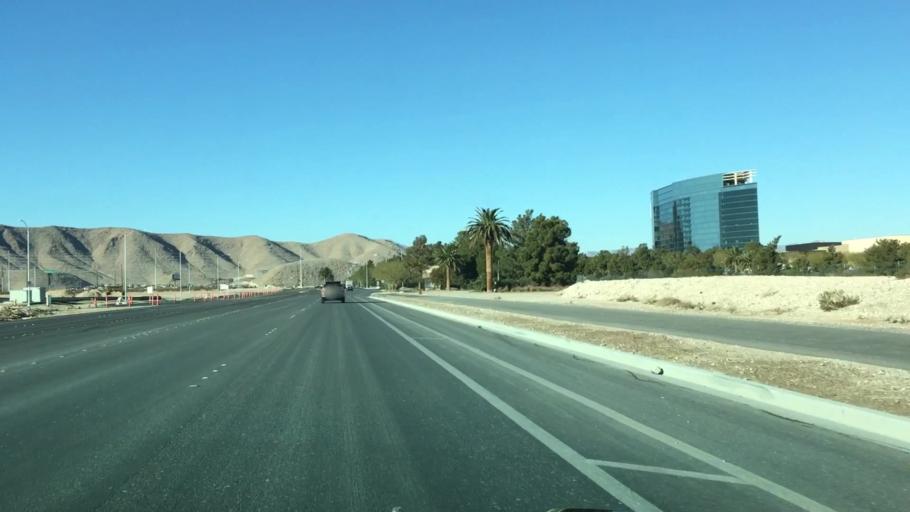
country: US
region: Nevada
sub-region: Clark County
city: Enterprise
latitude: 35.9629
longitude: -115.1646
